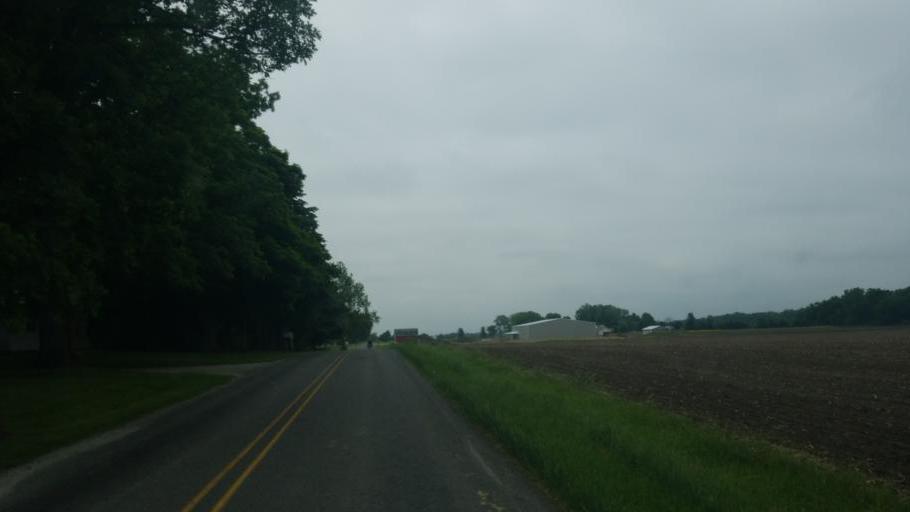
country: US
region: Indiana
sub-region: Elkhart County
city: Nappanee
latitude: 41.4622
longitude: -86.0497
